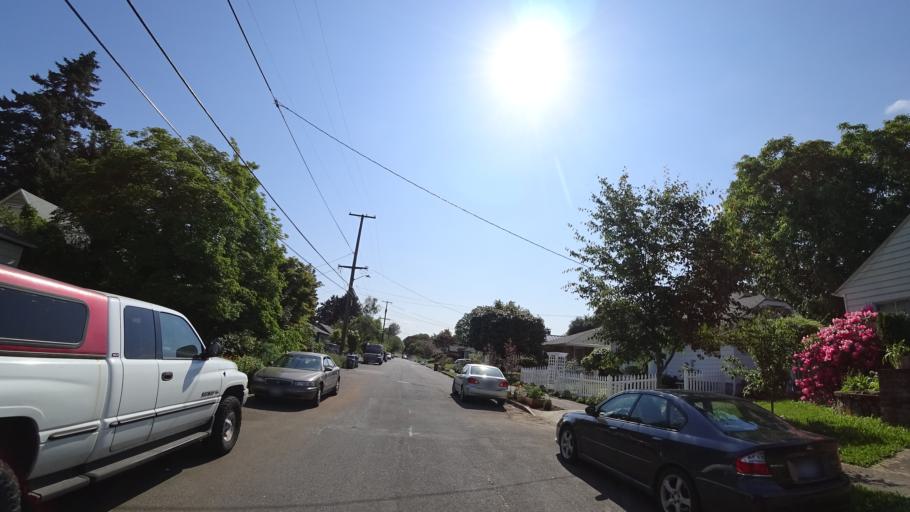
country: US
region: Oregon
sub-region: Multnomah County
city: Portland
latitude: 45.5732
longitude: -122.6460
